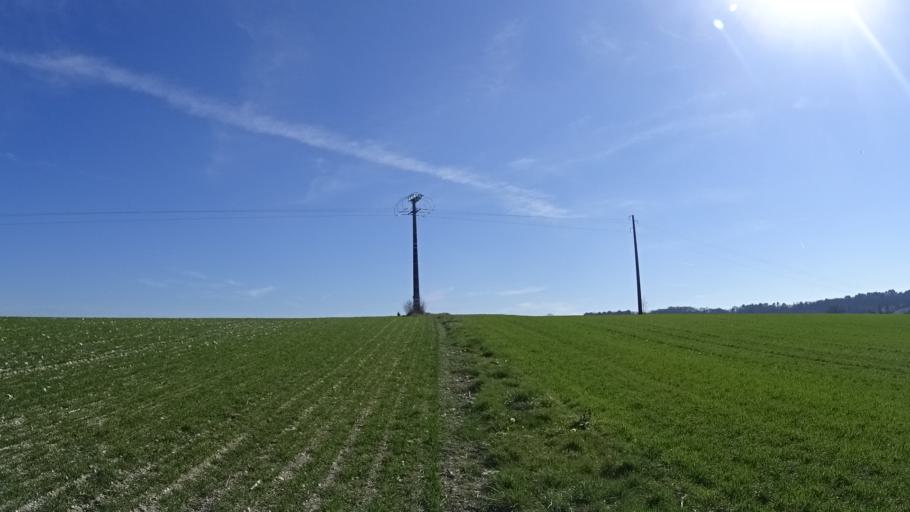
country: FR
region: Aquitaine
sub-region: Departement de la Dordogne
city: Riberac
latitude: 45.2275
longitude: 0.3374
